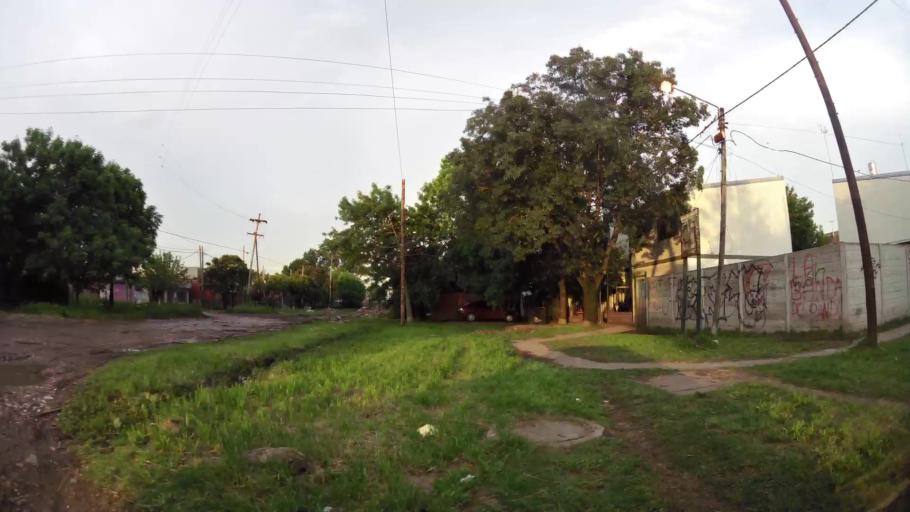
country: AR
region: Buenos Aires
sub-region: Partido de Almirante Brown
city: Adrogue
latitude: -34.7573
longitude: -58.3420
